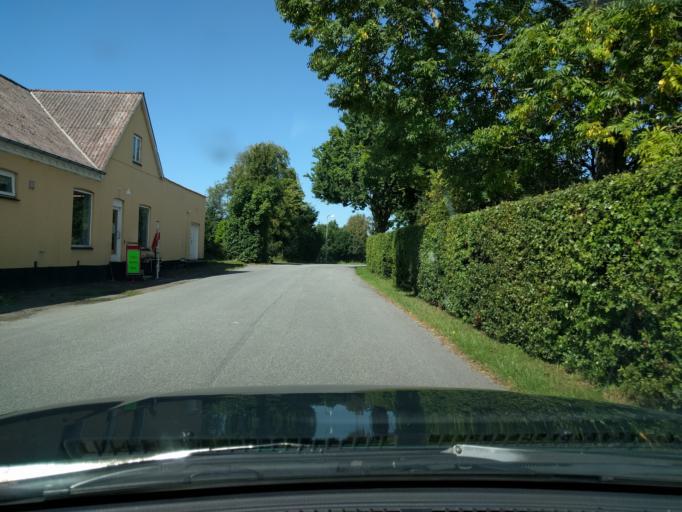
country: DK
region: Zealand
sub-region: Vordingborg Kommune
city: Orslev
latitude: 55.0782
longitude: 11.9479
